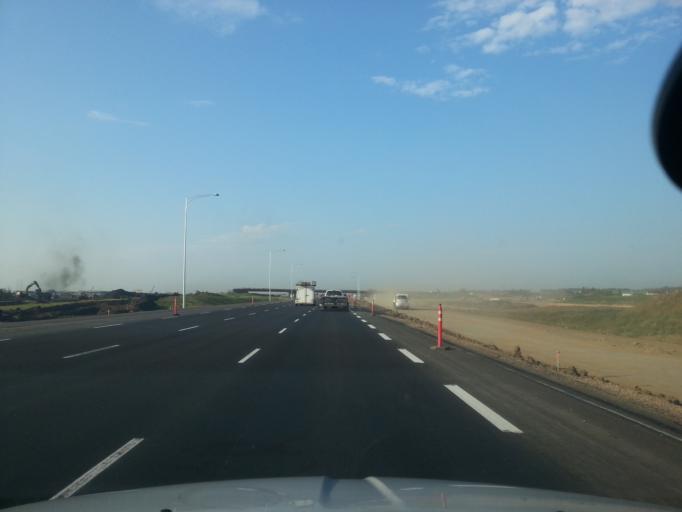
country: CA
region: Alberta
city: Beaumont
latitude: 53.4028
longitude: -113.5084
